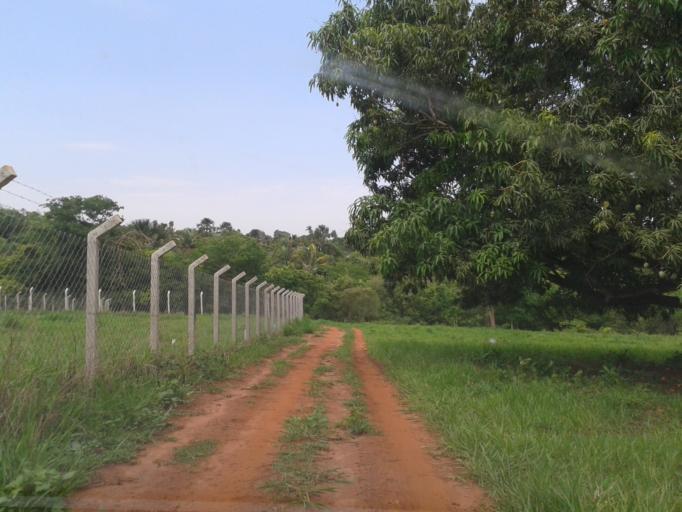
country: BR
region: Minas Gerais
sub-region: Ituiutaba
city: Ituiutaba
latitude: -18.9818
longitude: -49.4426
